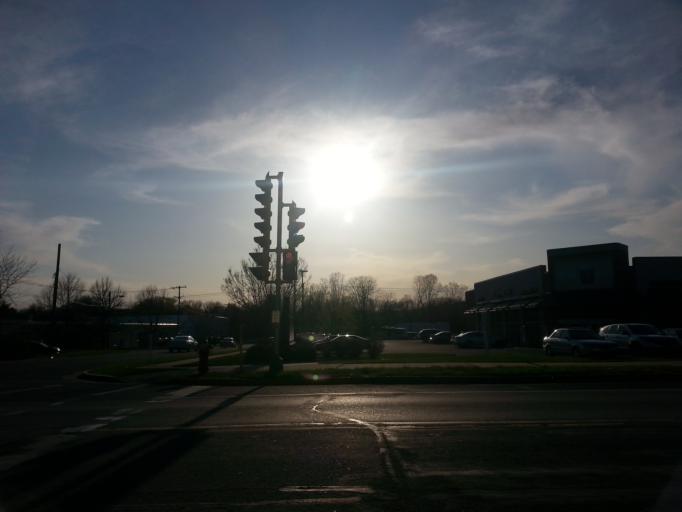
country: US
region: Wisconsin
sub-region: Pierce County
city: River Falls
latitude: 44.8700
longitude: -92.6218
